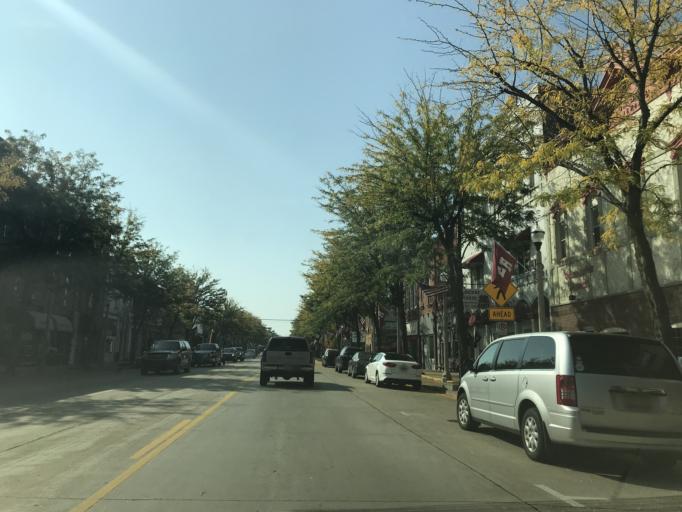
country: US
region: Michigan
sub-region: Eaton County
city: Eaton Rapids
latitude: 42.5125
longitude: -84.6558
